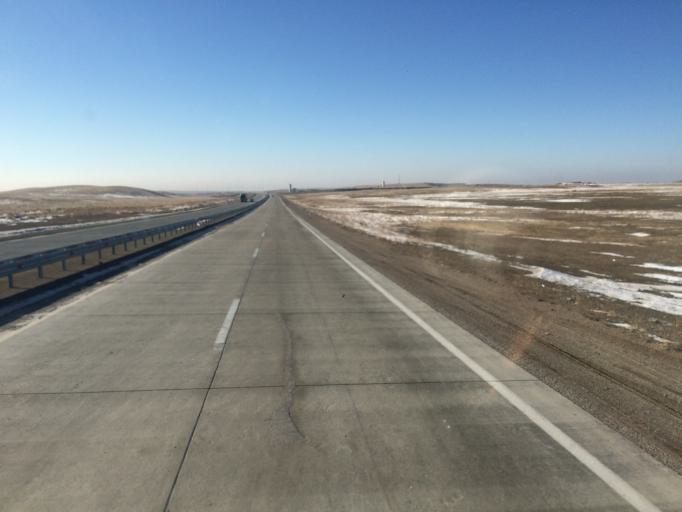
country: KZ
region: Zhambyl
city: Georgiyevka
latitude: 43.3562
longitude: 74.5823
